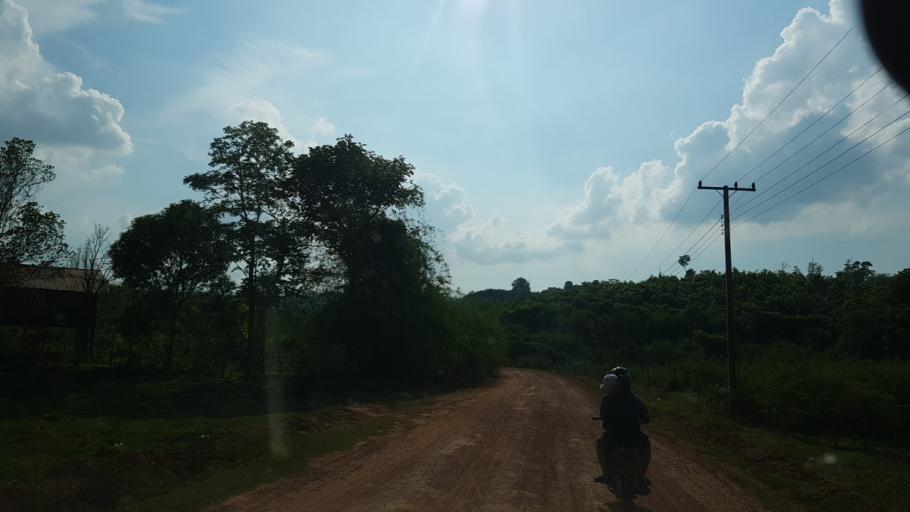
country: LA
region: Vientiane
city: Muang Phon-Hong
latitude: 18.3521
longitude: 102.2790
